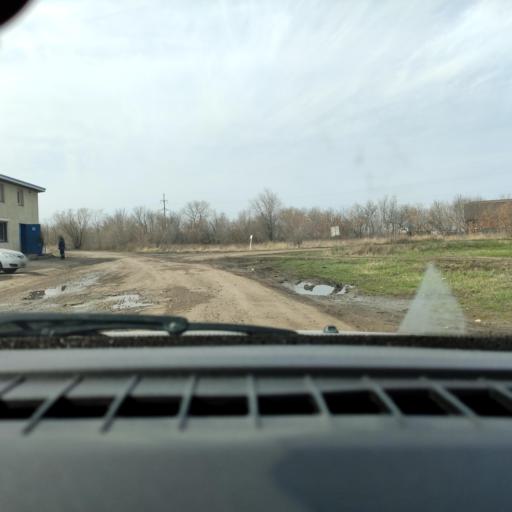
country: RU
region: Samara
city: Dubovyy Umet
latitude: 53.0934
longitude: 50.3067
